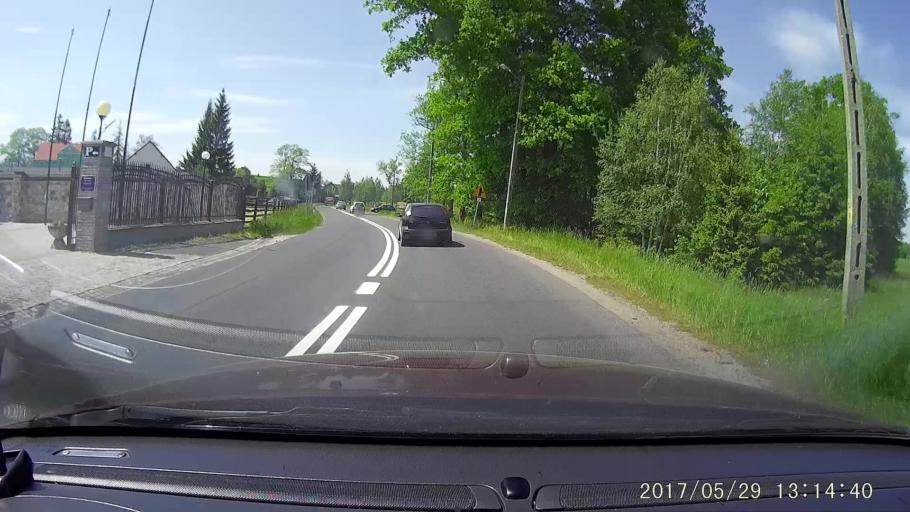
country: PL
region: Lower Silesian Voivodeship
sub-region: Powiat lwowecki
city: Lubomierz
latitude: 50.9811
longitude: 15.4875
